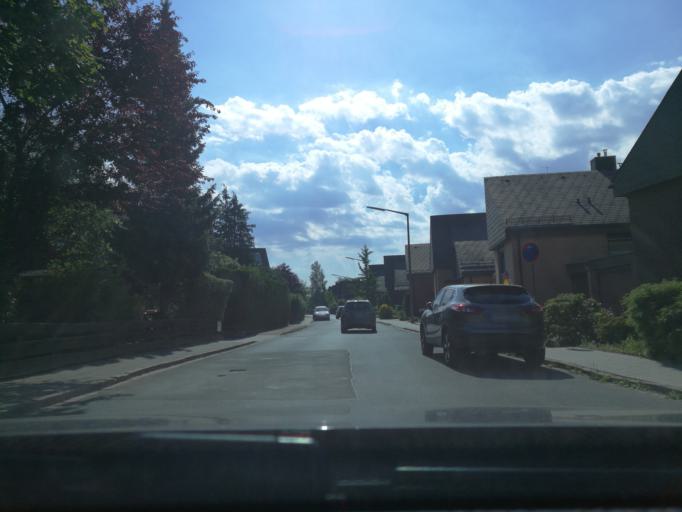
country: DE
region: Bavaria
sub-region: Regierungsbezirk Mittelfranken
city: Schwarzenbruck
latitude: 49.3580
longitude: 11.2297
